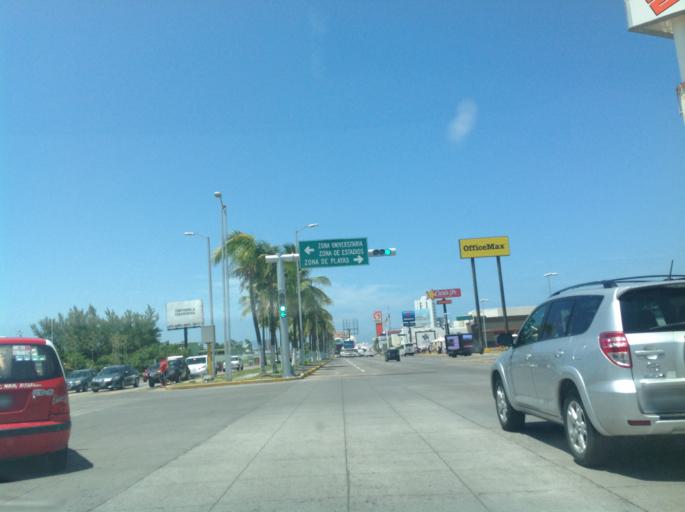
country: MX
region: Veracruz
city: Veracruz
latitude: 19.1595
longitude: -96.1091
